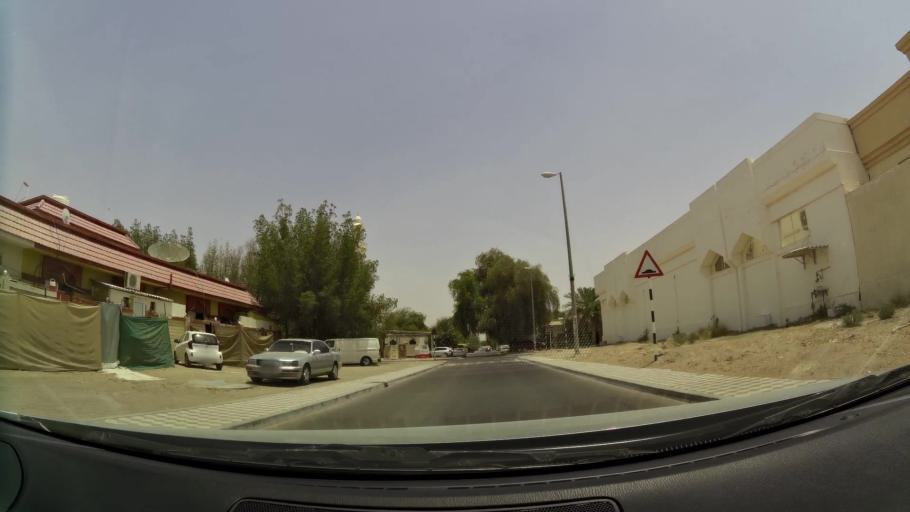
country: AE
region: Abu Dhabi
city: Al Ain
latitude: 24.2027
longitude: 55.7791
